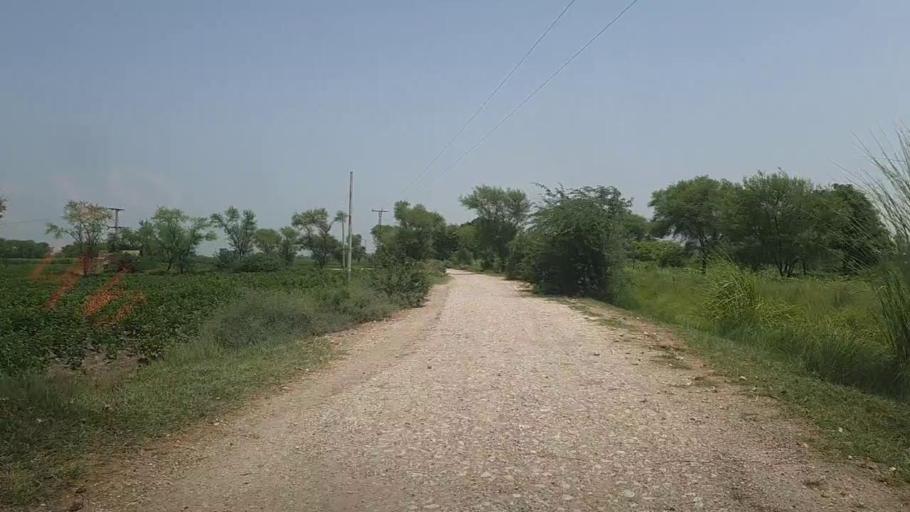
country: PK
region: Sindh
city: Pad Idan
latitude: 26.8457
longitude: 68.2954
